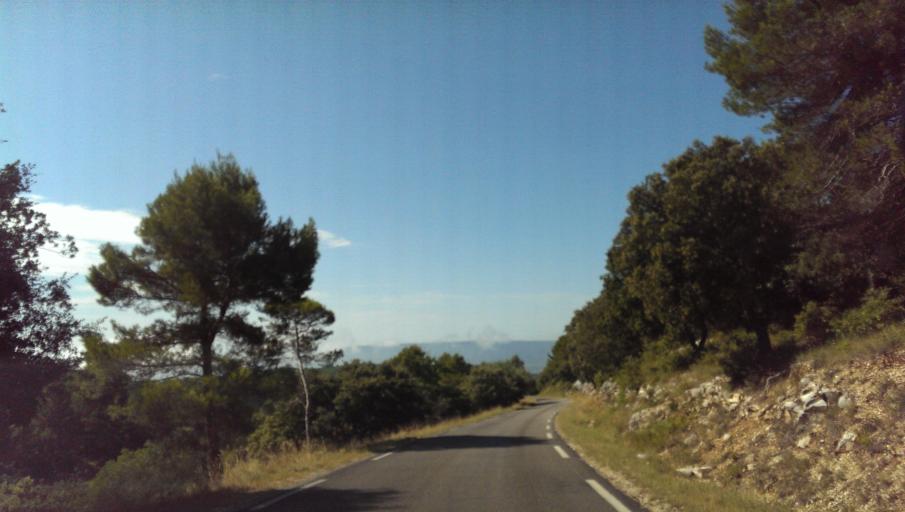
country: FR
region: Provence-Alpes-Cote d'Azur
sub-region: Departement du Vaucluse
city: Gordes
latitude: 43.9490
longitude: 5.1958
